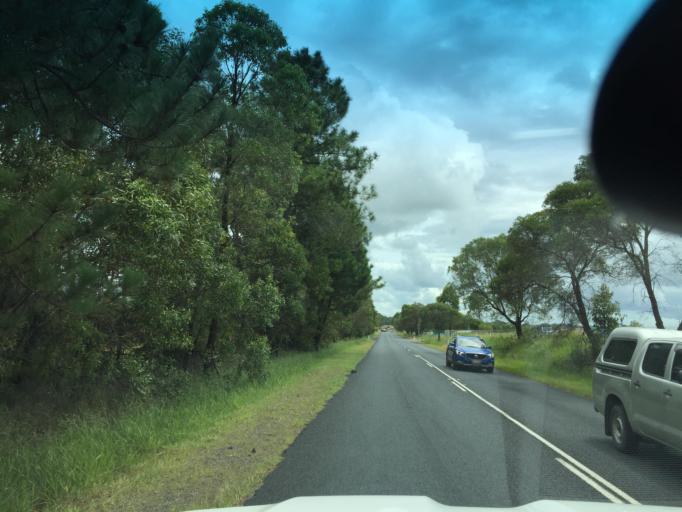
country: AU
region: Queensland
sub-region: Moreton Bay
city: Morayfield
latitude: -27.1139
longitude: 152.9799
